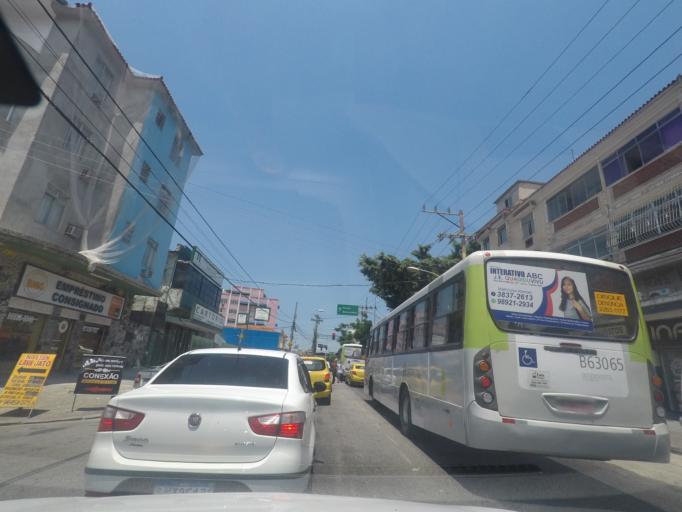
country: BR
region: Rio de Janeiro
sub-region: Duque De Caxias
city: Duque de Caxias
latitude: -22.8395
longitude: -43.2969
